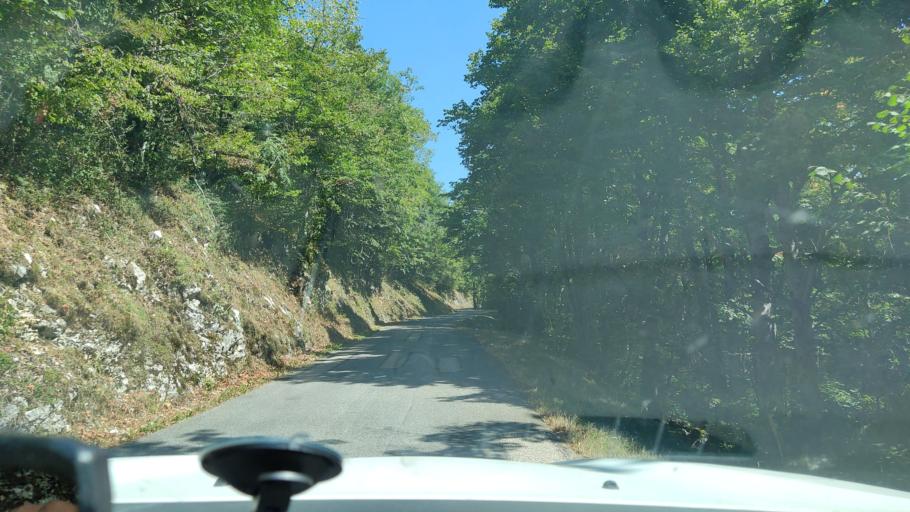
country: FR
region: Rhone-Alpes
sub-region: Departement de la Savoie
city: Le Bourget-du-Lac
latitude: 45.6577
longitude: 5.8354
